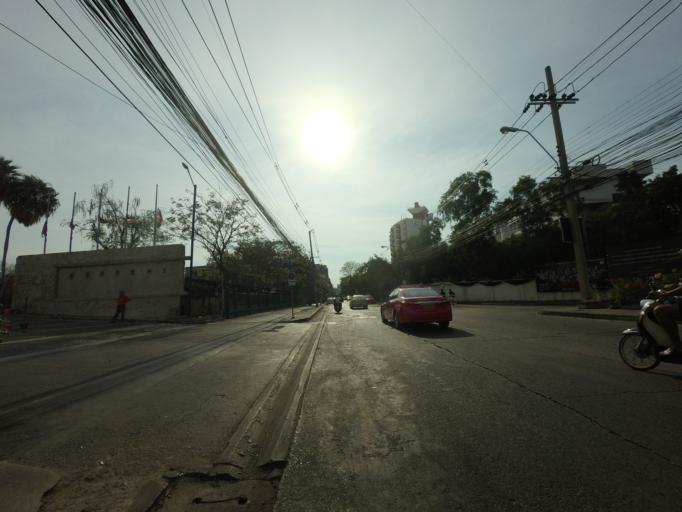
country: TH
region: Bangkok
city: Bang Kapi
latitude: 13.7546
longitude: 100.6254
